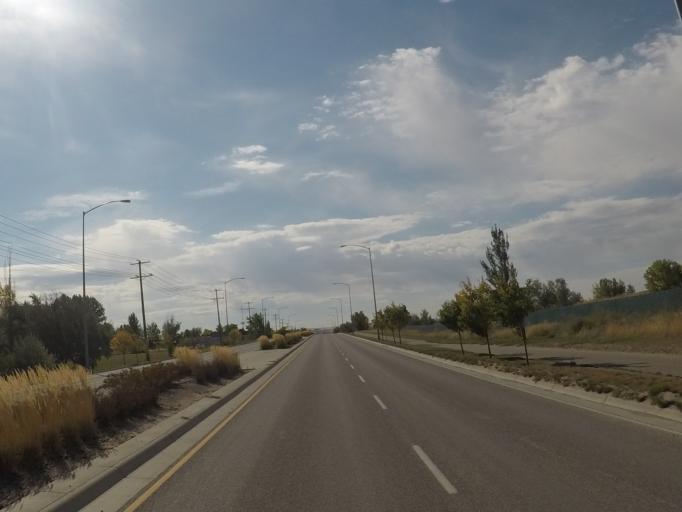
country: US
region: Montana
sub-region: Yellowstone County
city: Billings
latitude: 45.7462
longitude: -108.6176
